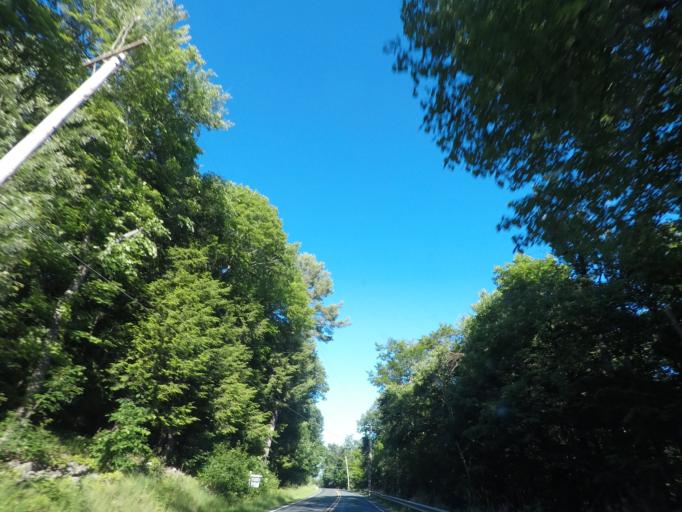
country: US
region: New York
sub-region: Rensselaer County
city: Averill Park
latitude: 42.5877
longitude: -73.5777
